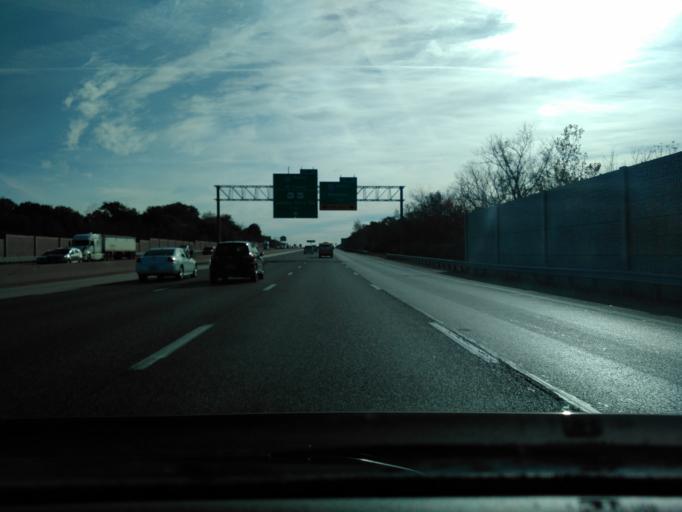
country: US
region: Missouri
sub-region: Saint Louis County
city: Concord
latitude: 38.5110
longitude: -90.3642
